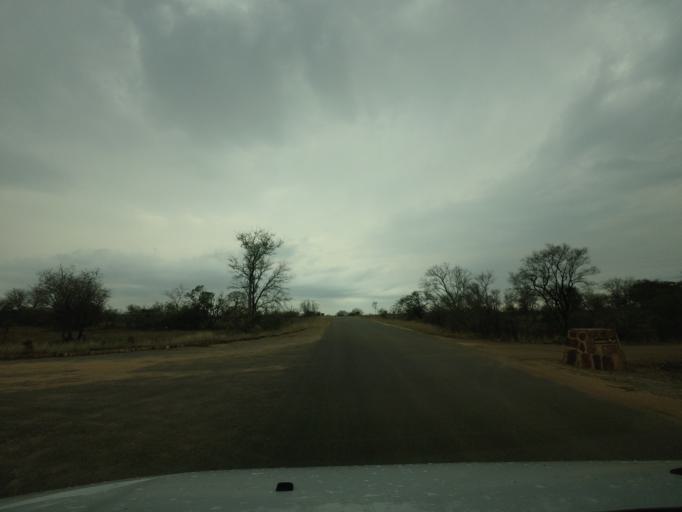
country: ZA
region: Limpopo
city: Thulamahashi
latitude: -24.4673
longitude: 31.4548
